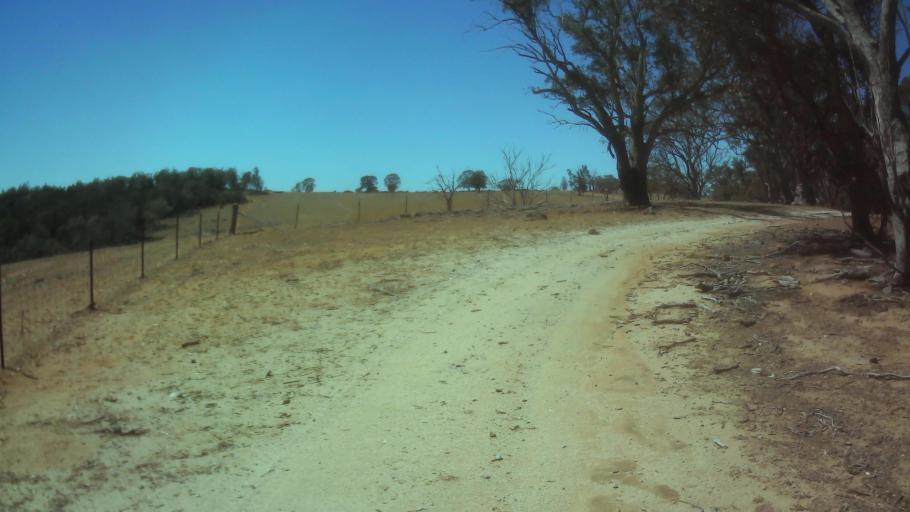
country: AU
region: New South Wales
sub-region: Cowra
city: Cowra
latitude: -33.8968
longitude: 148.5062
